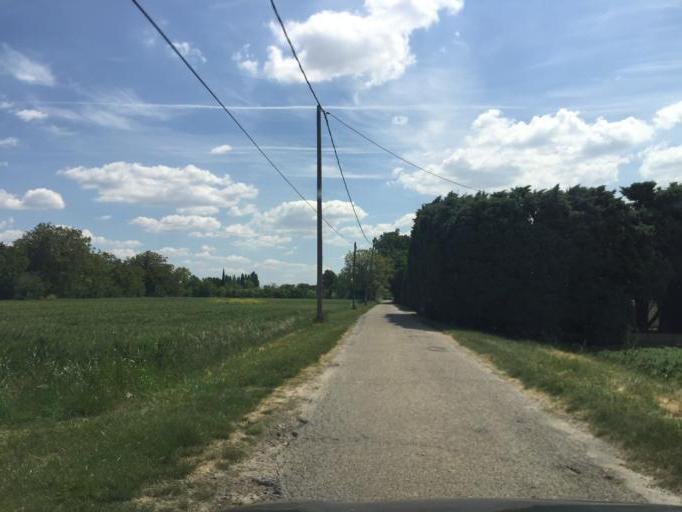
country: FR
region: Provence-Alpes-Cote d'Azur
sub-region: Departement du Vaucluse
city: Jonquieres
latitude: 44.1293
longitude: 4.8910
